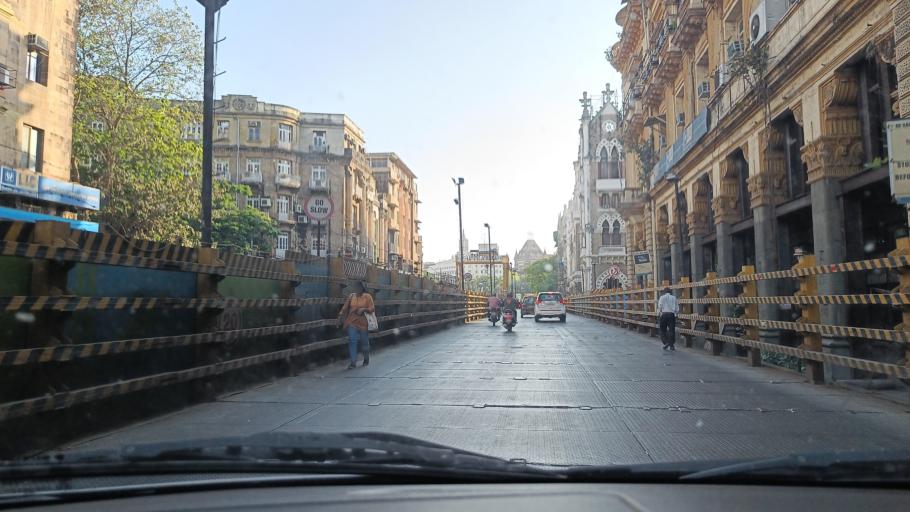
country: IN
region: Maharashtra
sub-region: Raigarh
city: Uran
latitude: 18.9351
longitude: 72.8330
